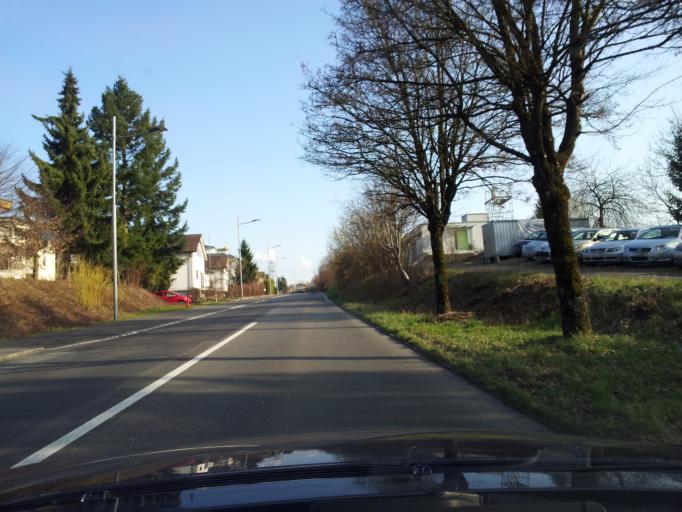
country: CH
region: Aargau
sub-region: Bezirk Baden
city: Niederrohrdorf
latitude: 47.4172
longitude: 8.3168
